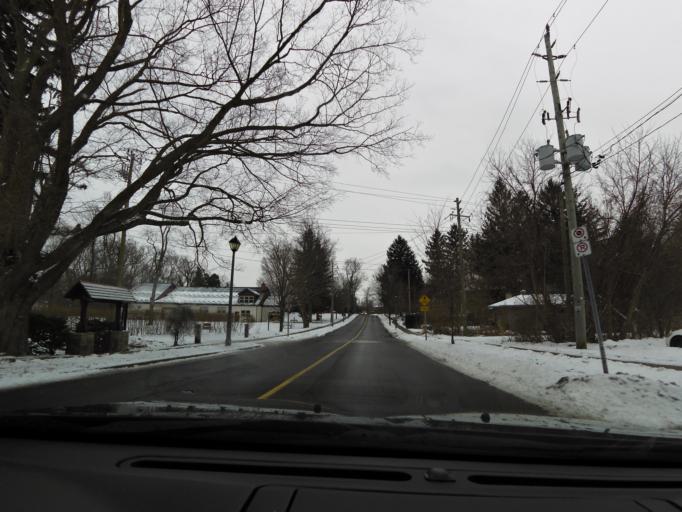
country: CA
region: Ontario
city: Ancaster
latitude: 43.2236
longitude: -79.9779
